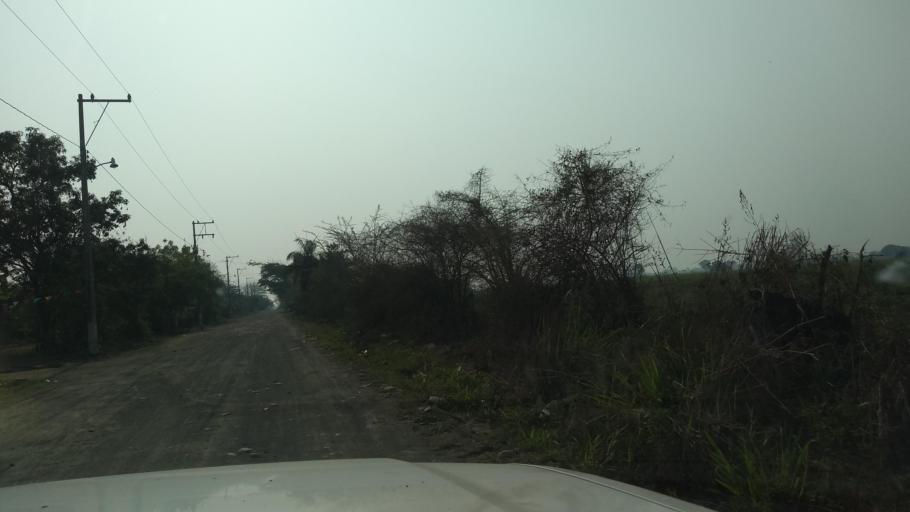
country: MX
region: Oaxaca
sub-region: Cosolapa
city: Cosolapa
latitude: 18.6225
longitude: -96.6041
